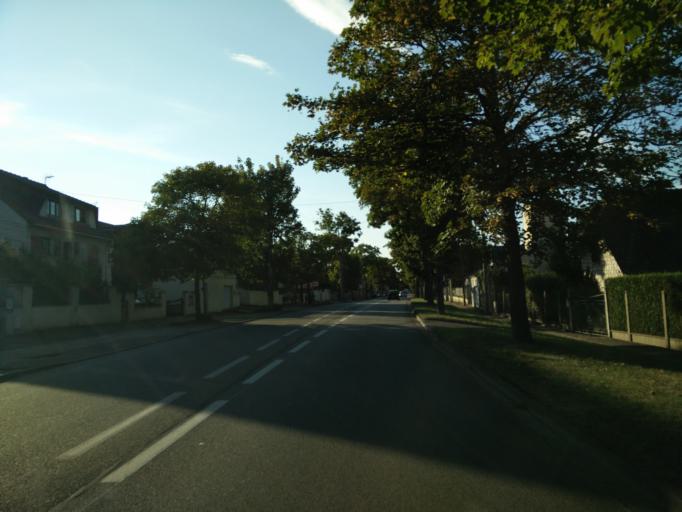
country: FR
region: Haute-Normandie
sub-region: Departement de l'Eure
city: Vernon
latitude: 49.0836
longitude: 1.5008
